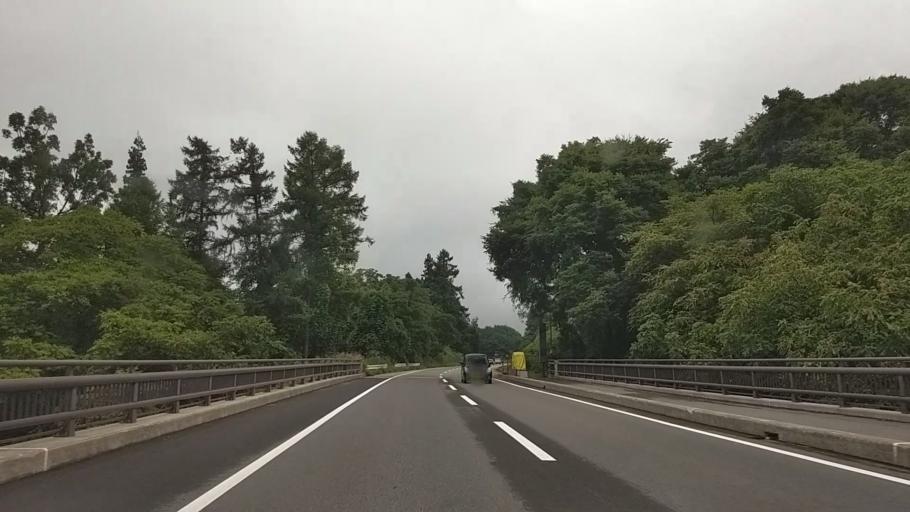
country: JP
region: Nagano
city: Iiyama
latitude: 36.8172
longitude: 138.3443
